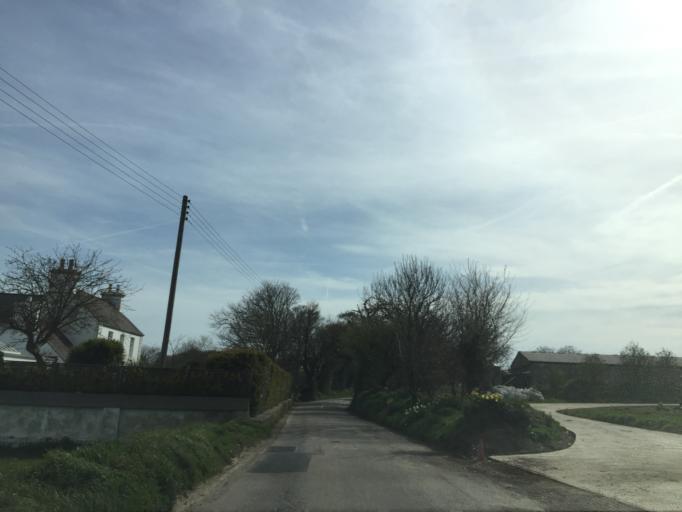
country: JE
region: St Helier
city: Saint Helier
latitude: 49.2289
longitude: -2.0392
